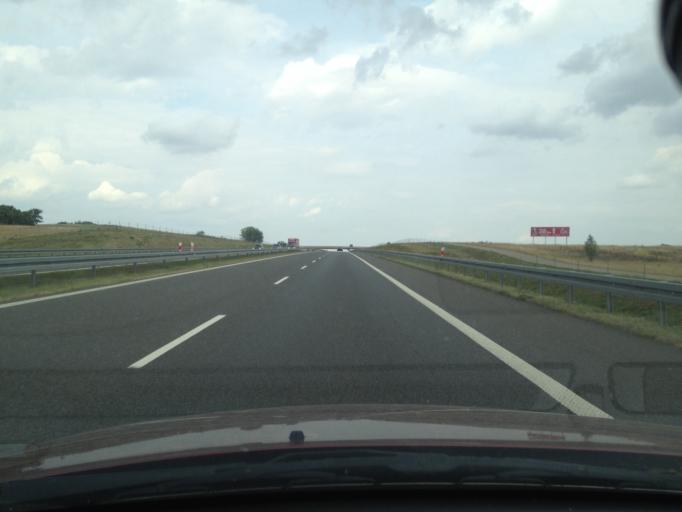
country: PL
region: West Pomeranian Voivodeship
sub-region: Powiat pyrzycki
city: Kozielice
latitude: 53.0258
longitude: 14.8628
